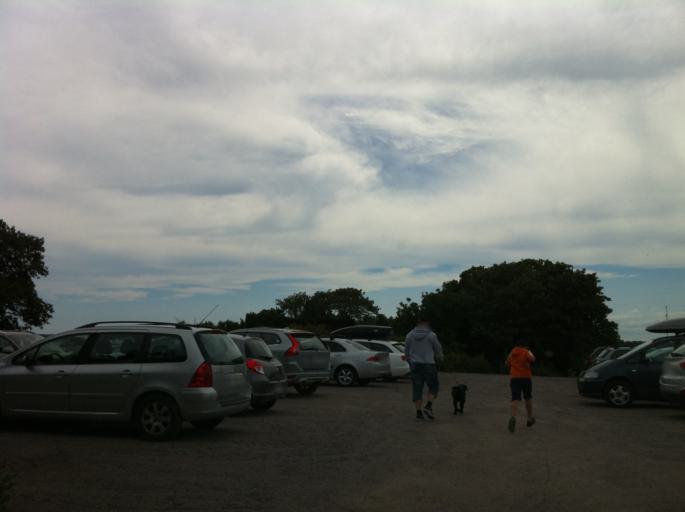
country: SE
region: Kalmar
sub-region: Vasterviks Kommun
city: Vaestervik
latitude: 57.3674
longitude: 17.0899
